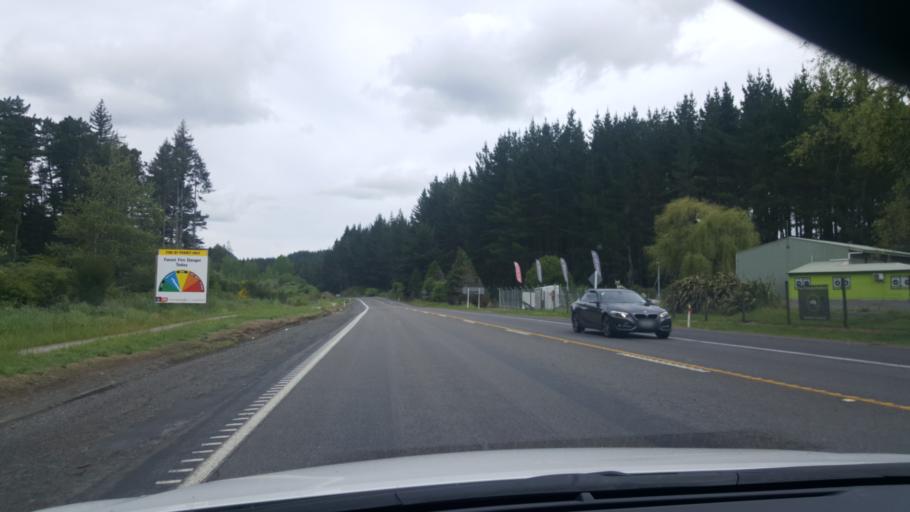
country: NZ
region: Bay of Plenty
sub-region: Rotorua District
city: Rotorua
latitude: -38.1790
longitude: 176.2495
